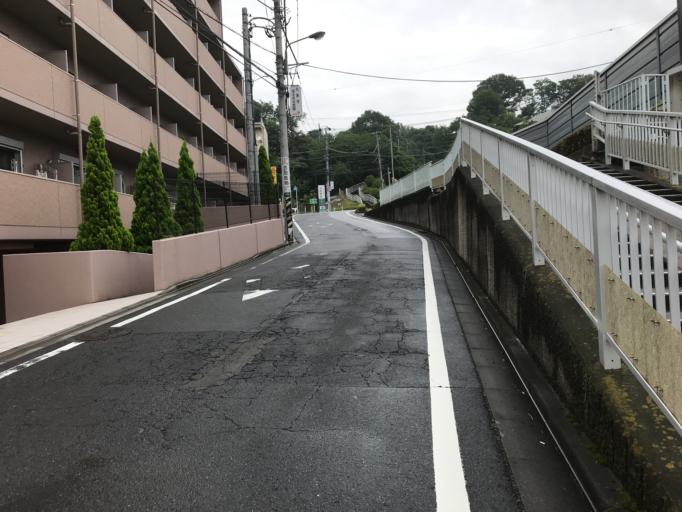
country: JP
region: Tokyo
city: Hachioji
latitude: 35.6679
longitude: 139.3410
